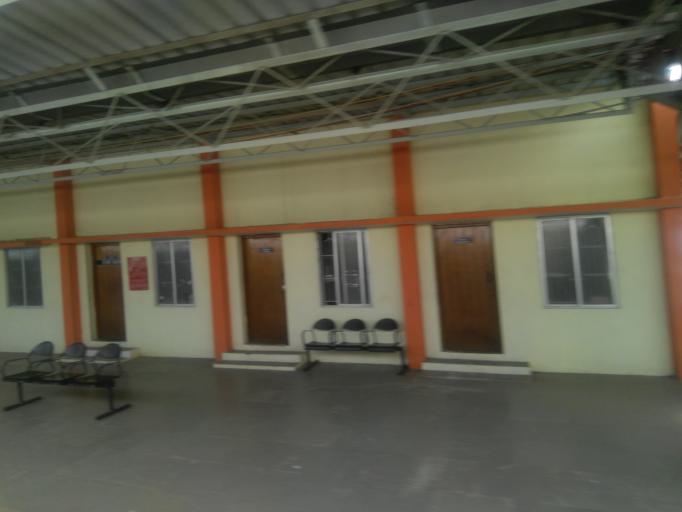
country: IN
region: Tamil Nadu
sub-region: Coimbatore
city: Coimbatore
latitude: 11.0204
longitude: 76.9546
